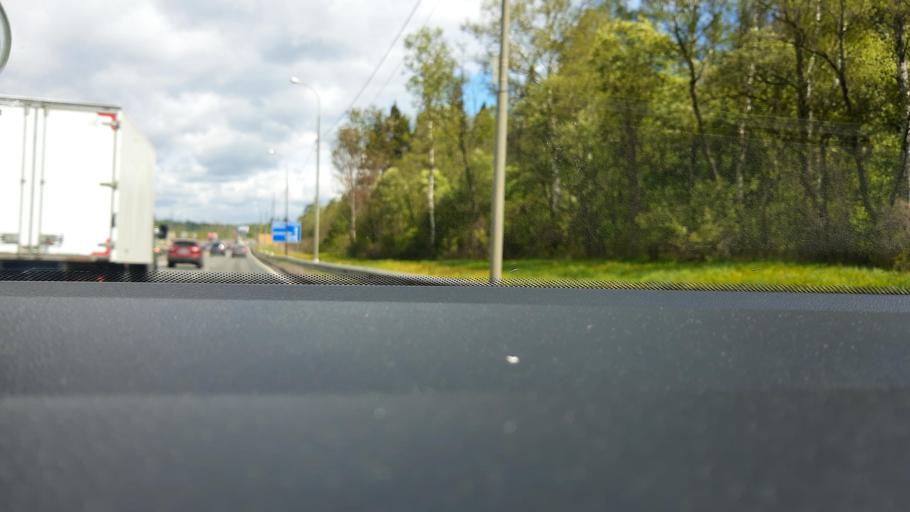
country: RU
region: Moskovskaya
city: Podosinki
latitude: 56.2140
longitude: 37.5217
